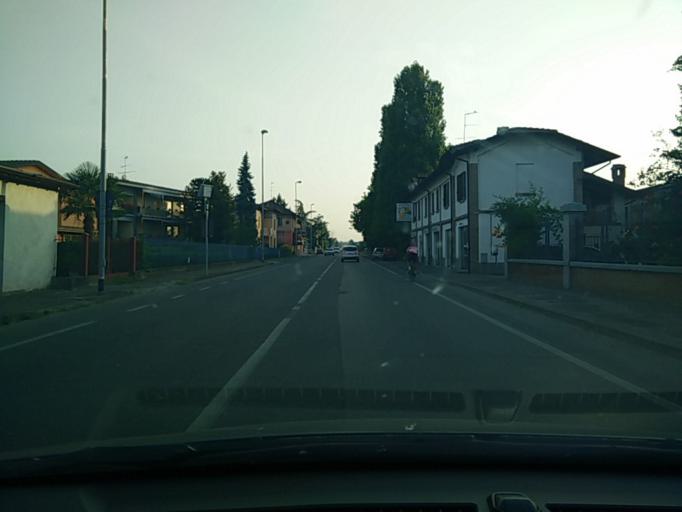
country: IT
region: Lombardy
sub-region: Provincia di Pavia
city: Santa Giuletta
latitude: 45.0350
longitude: 9.1798
